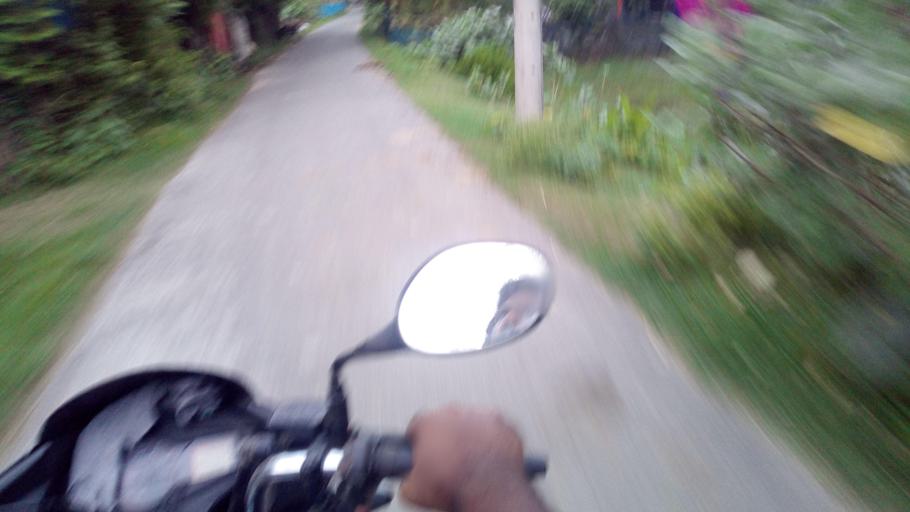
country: BD
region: Khulna
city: Phultala
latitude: 22.7539
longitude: 89.4050
